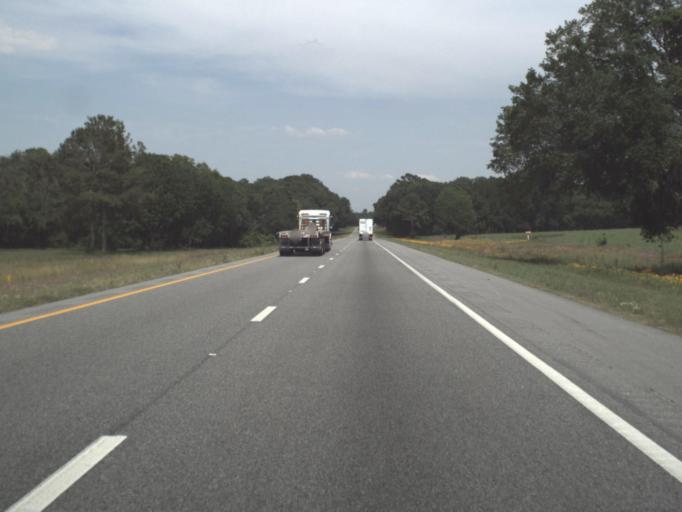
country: US
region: Florida
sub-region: Suwannee County
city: Live Oak
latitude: 30.3505
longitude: -83.0482
